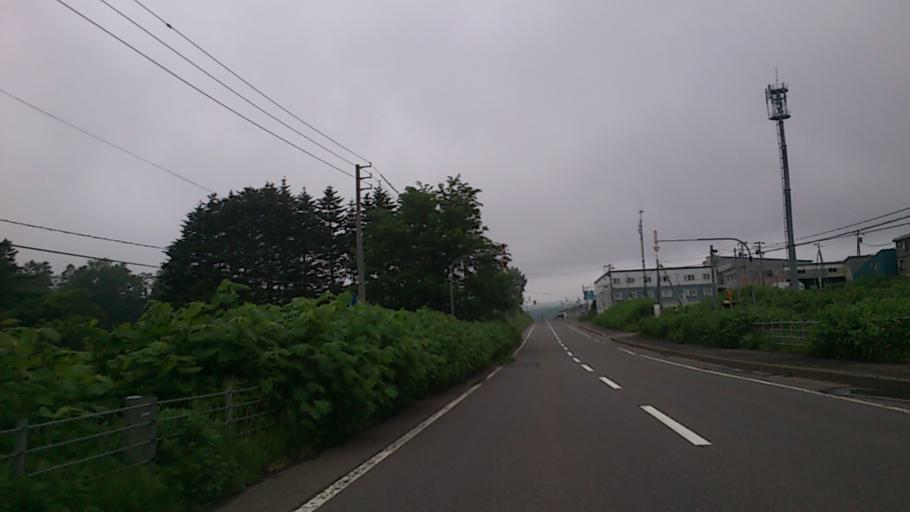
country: JP
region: Hokkaido
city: Niseko Town
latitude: 42.8500
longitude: 140.8903
